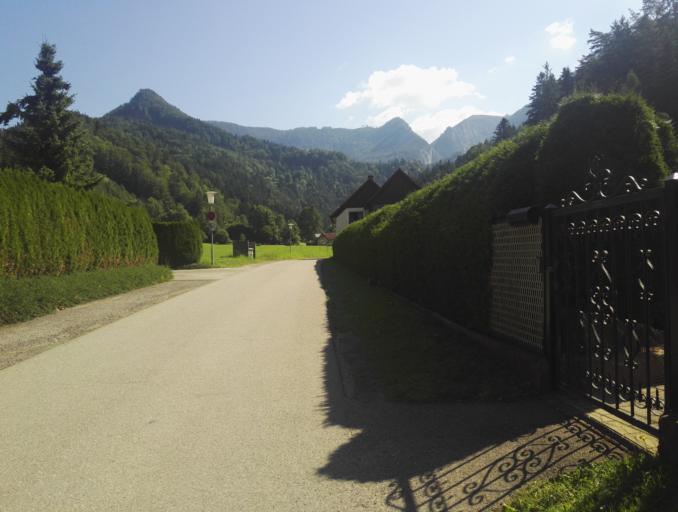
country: AT
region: Styria
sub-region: Politischer Bezirk Graz-Umgebung
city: Rothelstein
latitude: 47.3317
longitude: 15.3660
